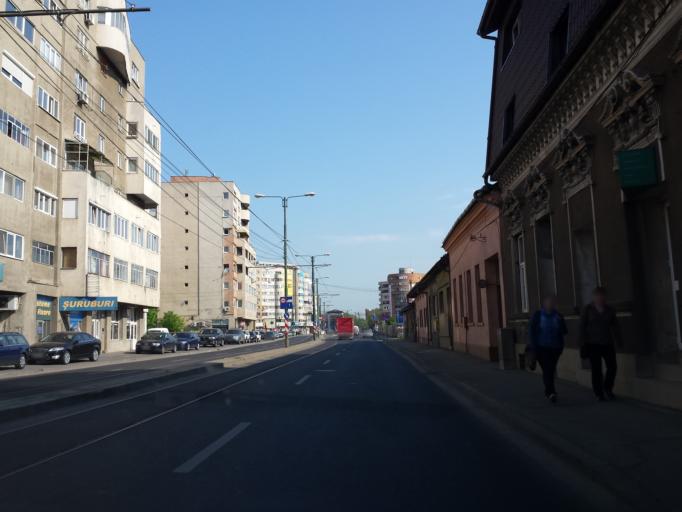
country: RO
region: Timis
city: Timisoara
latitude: 45.7634
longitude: 21.2608
